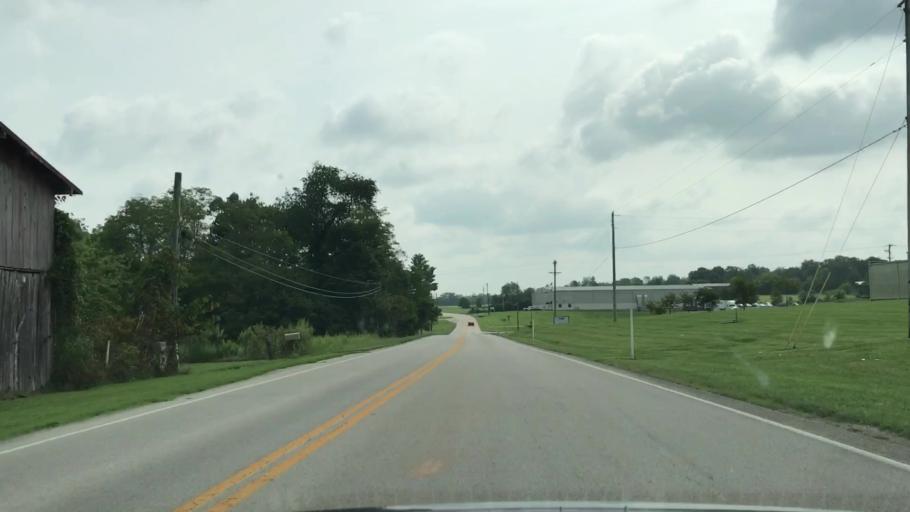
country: US
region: Kentucky
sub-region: Barren County
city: Cave City
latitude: 37.0903
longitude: -86.0753
